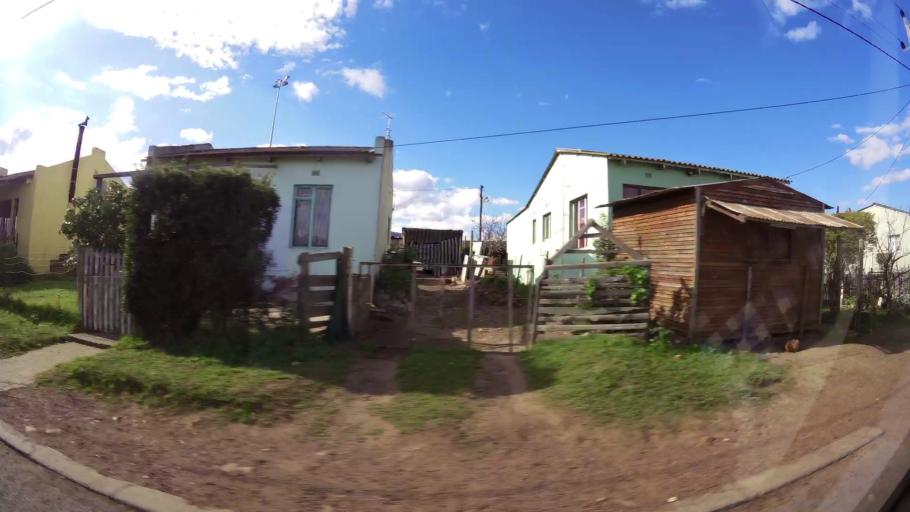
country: ZA
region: Western Cape
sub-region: Overberg District Municipality
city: Swellendam
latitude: -34.0395
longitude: 20.4432
